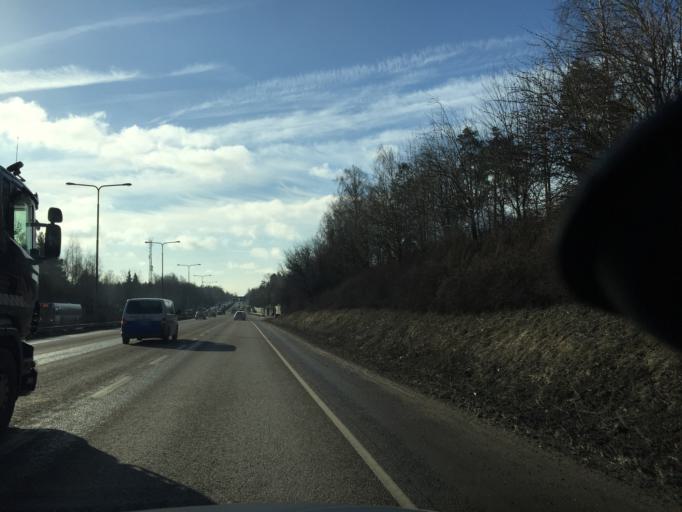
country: FI
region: Uusimaa
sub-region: Helsinki
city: Teekkarikylae
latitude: 60.2426
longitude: 24.8926
